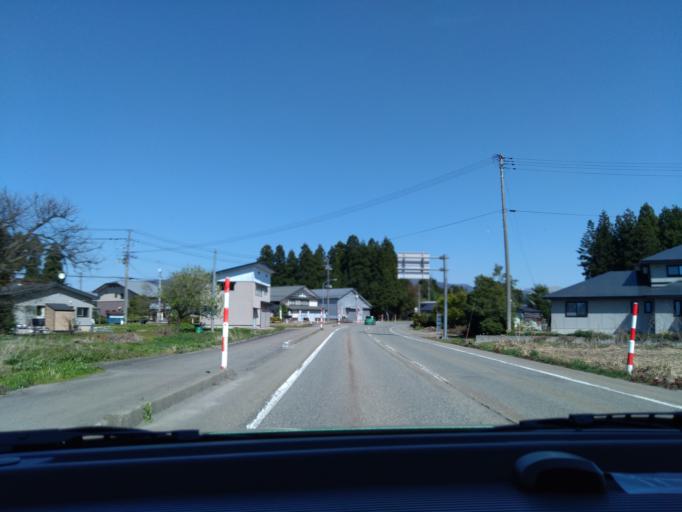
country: JP
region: Akita
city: Kakunodatemachi
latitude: 39.5760
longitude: 140.5675
